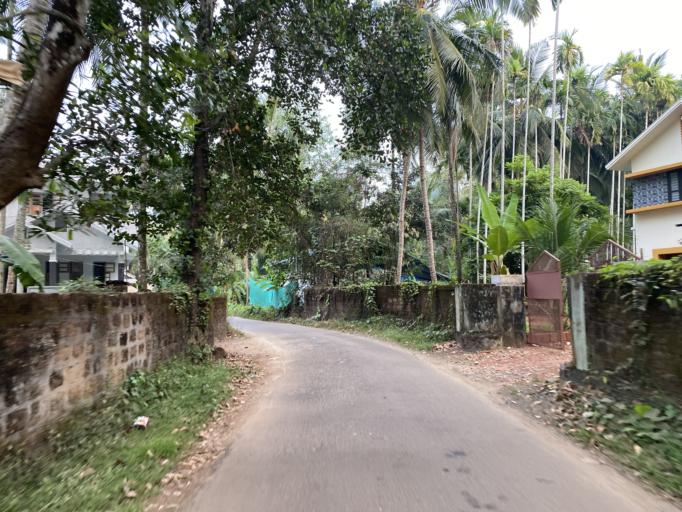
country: IN
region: Kerala
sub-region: Malappuram
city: Malappuram
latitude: 11.0472
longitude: 76.0069
